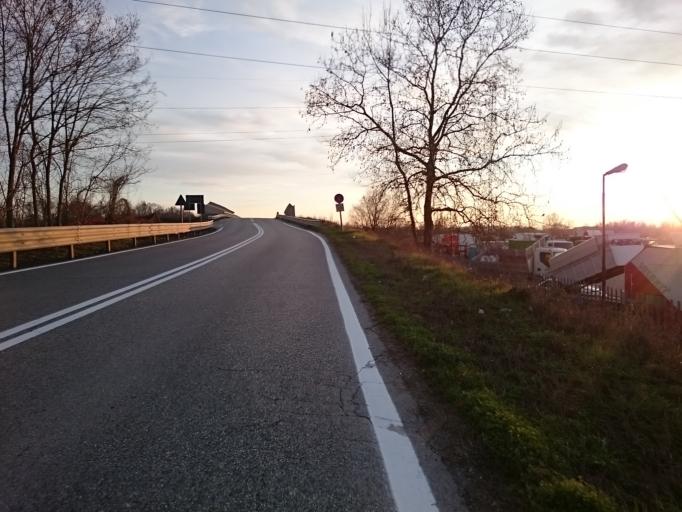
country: IT
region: Veneto
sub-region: Provincia di Verona
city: Castelnuovo del Garda
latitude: 45.4278
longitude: 10.7568
